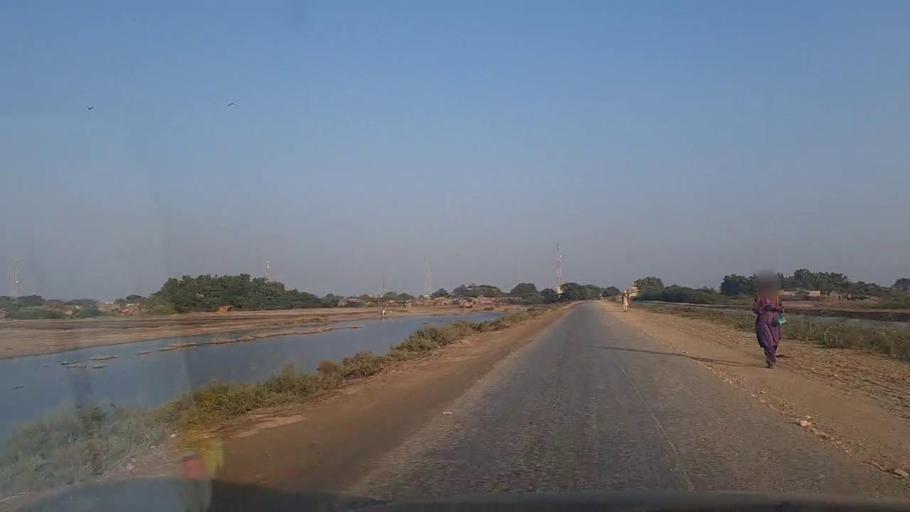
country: PK
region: Sindh
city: Keti Bandar
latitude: 24.3010
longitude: 67.5979
